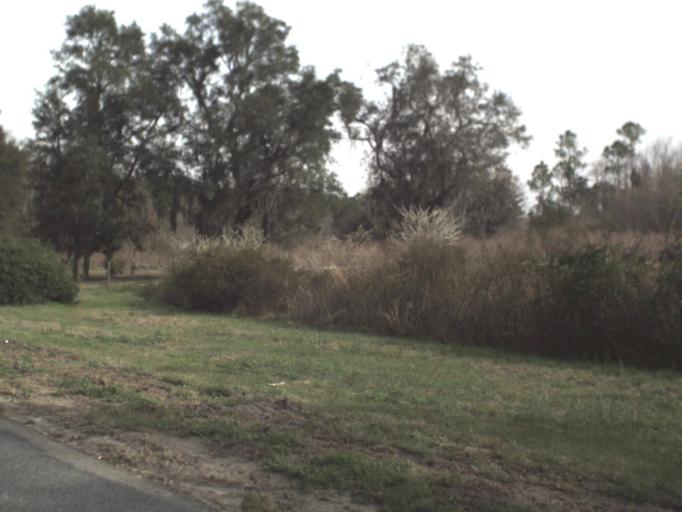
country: US
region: Florida
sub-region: Jefferson County
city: Monticello
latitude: 30.5012
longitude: -83.7526
